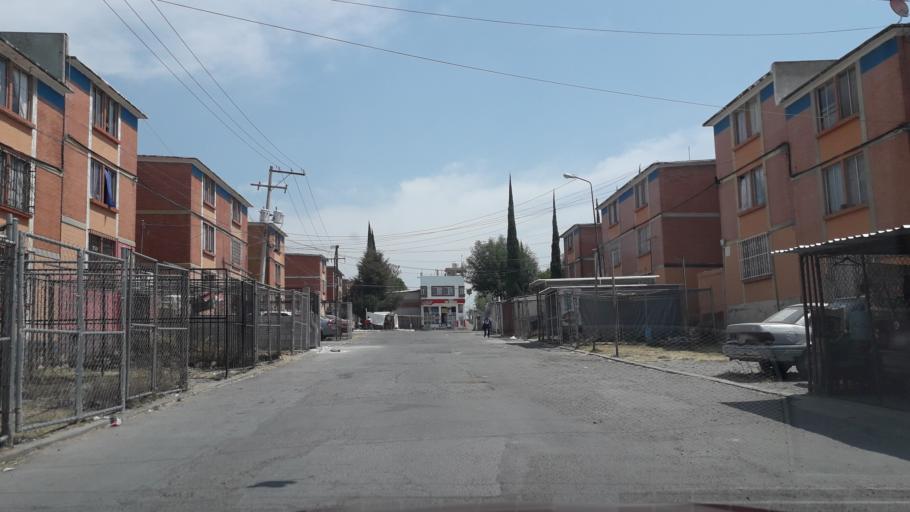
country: MX
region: Puebla
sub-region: Puebla
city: El Capulo (La Quebradora)
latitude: 18.9670
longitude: -98.2637
